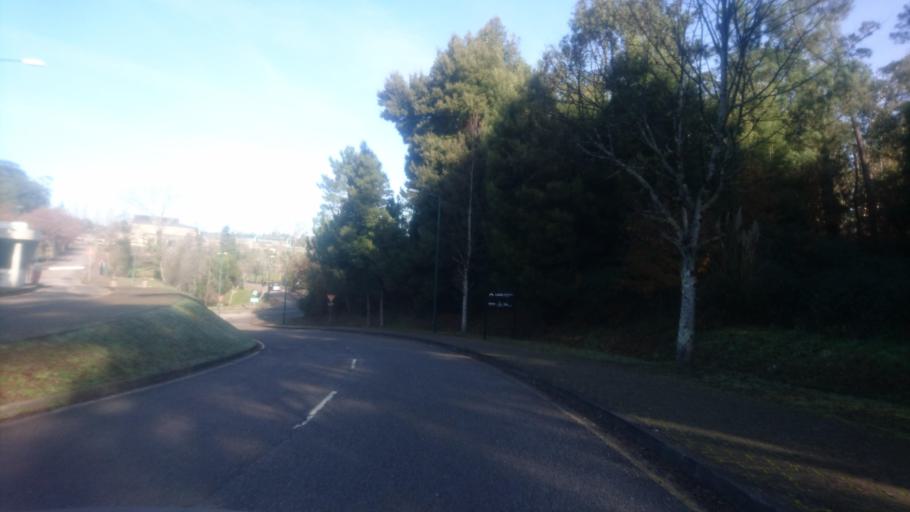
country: PT
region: Aveiro
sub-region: Santa Maria da Feira
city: Rio Meao
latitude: 40.9304
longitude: -8.5764
